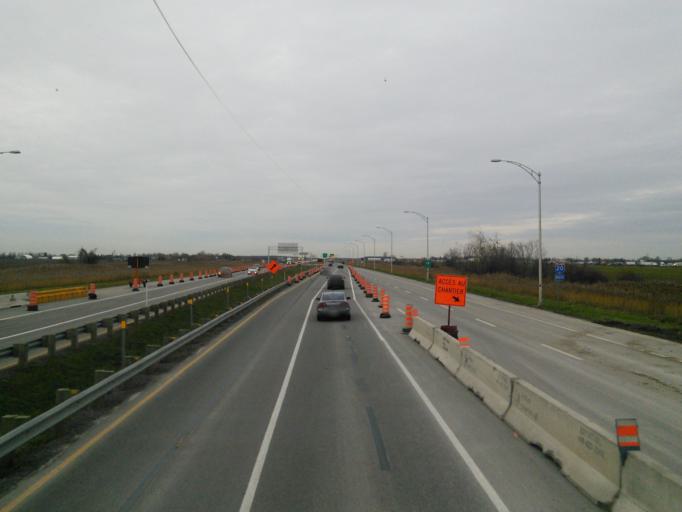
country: CA
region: Quebec
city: Les Cedres
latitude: 45.3489
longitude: -74.0676
